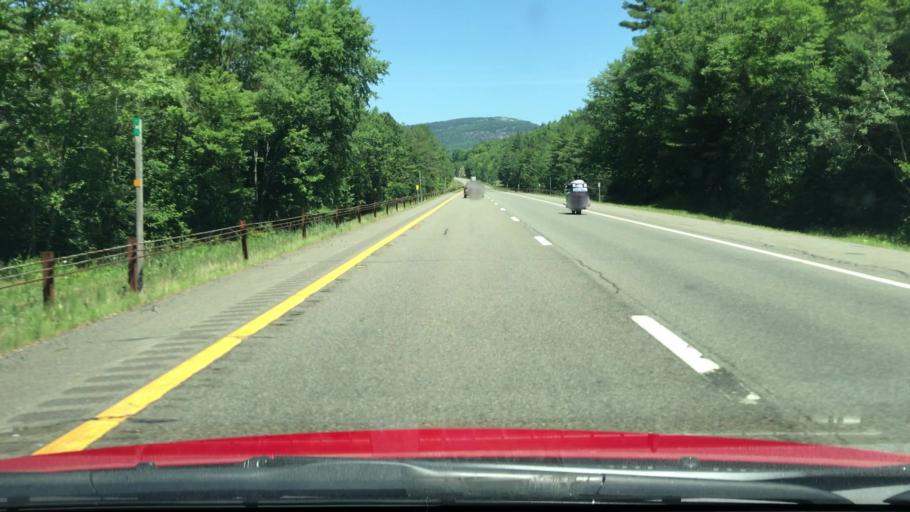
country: US
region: New York
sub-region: Essex County
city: Elizabethtown
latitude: 44.3555
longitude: -73.5323
